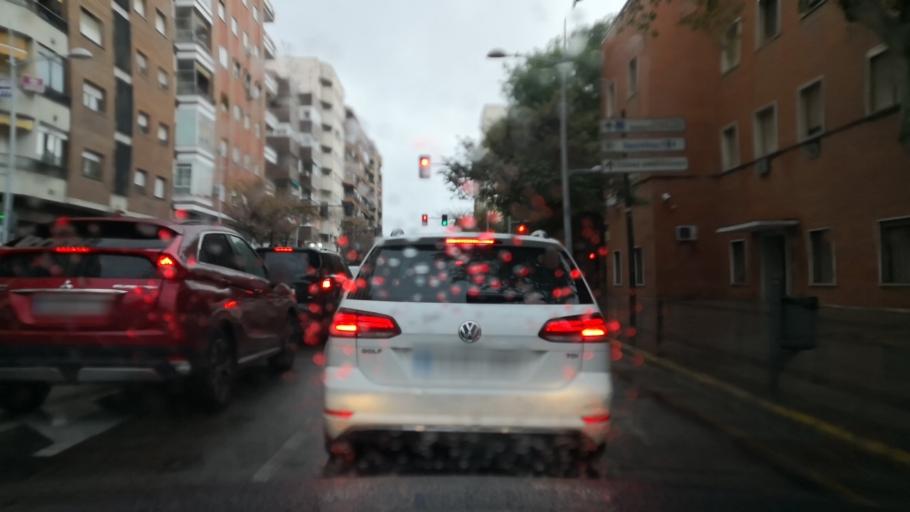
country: ES
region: Extremadura
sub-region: Provincia de Badajoz
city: Badajoz
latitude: 38.8715
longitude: -6.9730
